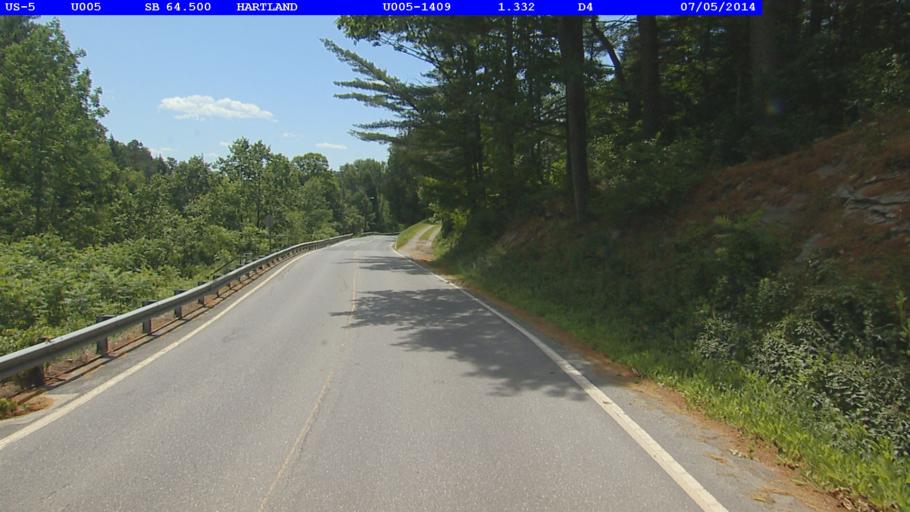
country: US
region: Vermont
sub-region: Windsor County
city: Windsor
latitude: 43.5376
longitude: -72.4017
